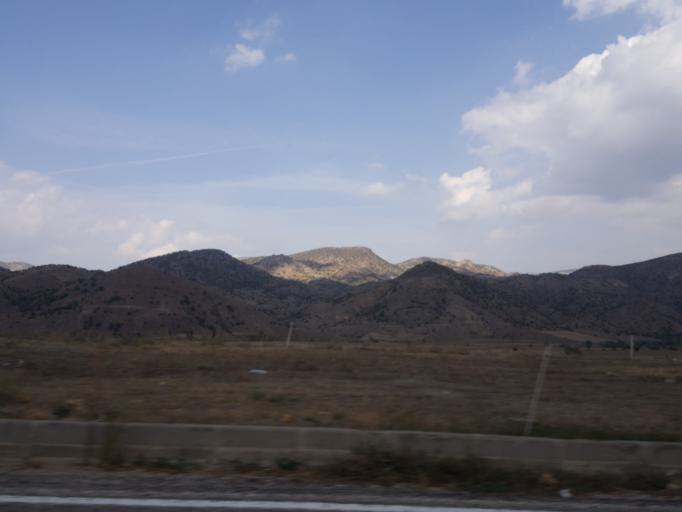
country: TR
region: Yozgat
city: Aydincik
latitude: 40.1753
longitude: 35.3678
